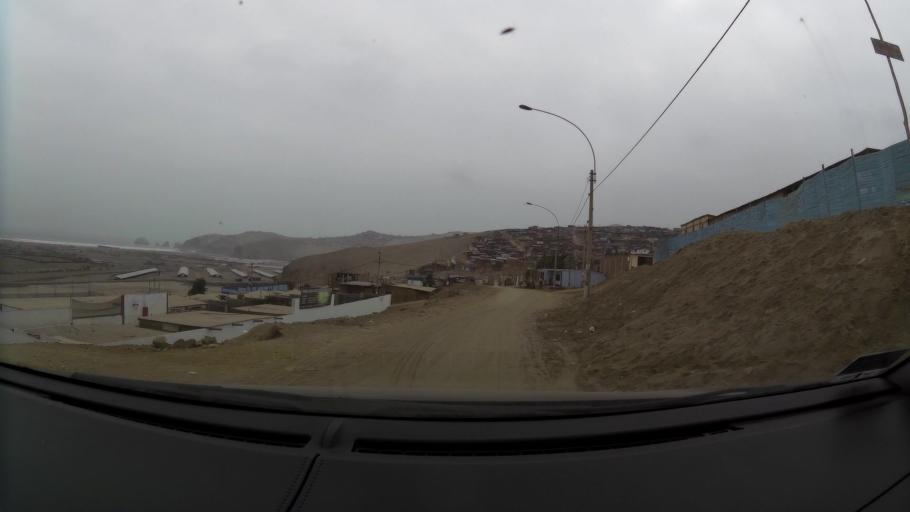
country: PE
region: Lima
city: Ventanilla
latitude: -11.8476
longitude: -77.1586
